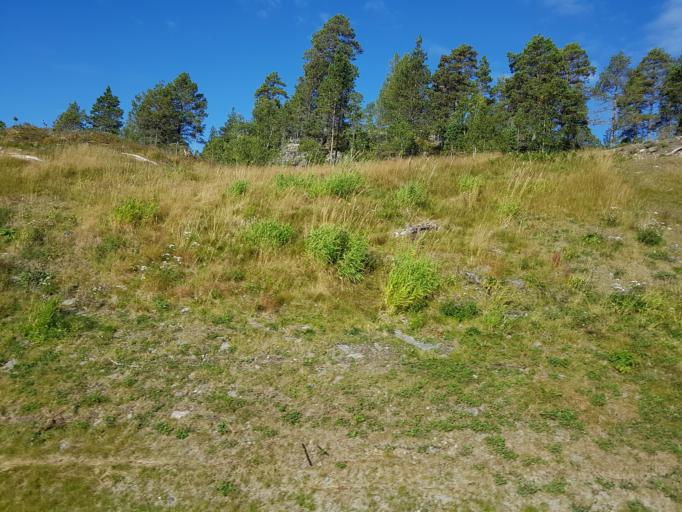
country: NO
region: Sor-Trondelag
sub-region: Trondheim
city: Trondheim
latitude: 63.6367
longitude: 10.2710
